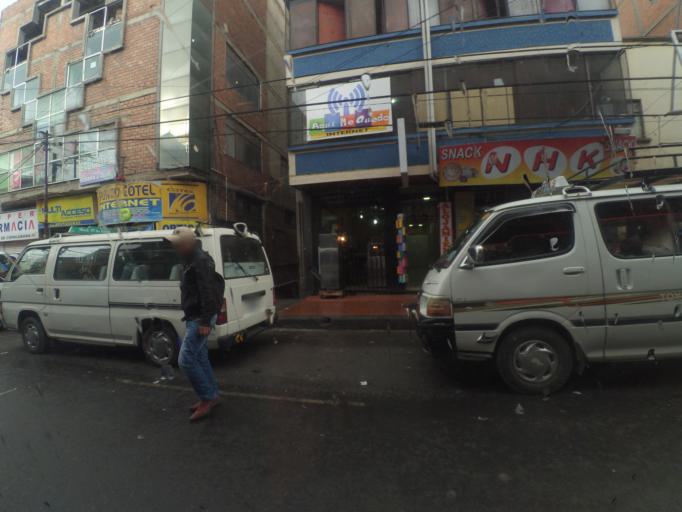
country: BO
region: La Paz
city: La Paz
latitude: -16.5063
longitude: -68.1621
